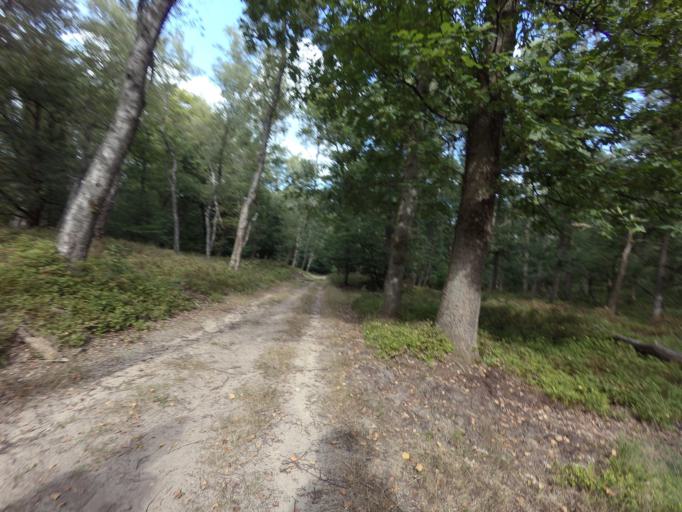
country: NL
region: Gelderland
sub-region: Gemeente Rheden
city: De Steeg
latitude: 52.0485
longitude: 6.0304
